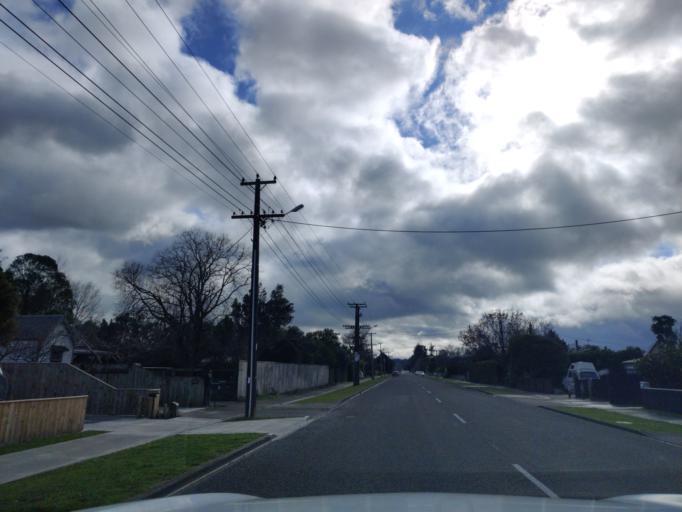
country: NZ
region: Manawatu-Wanganui
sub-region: Palmerston North City
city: Palmerston North
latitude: -40.2818
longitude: 175.7564
